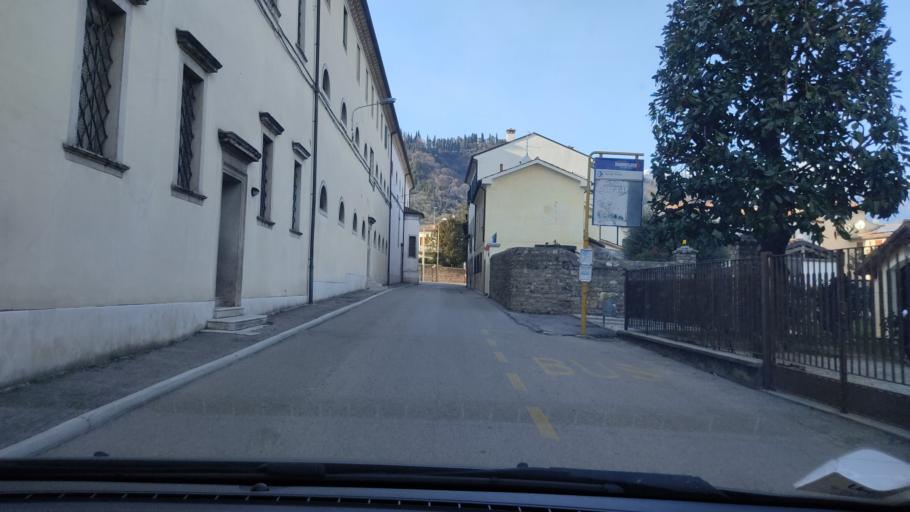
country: IT
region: Veneto
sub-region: Provincia di Treviso
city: Vittorio Veneto
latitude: 45.9735
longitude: 12.2949
